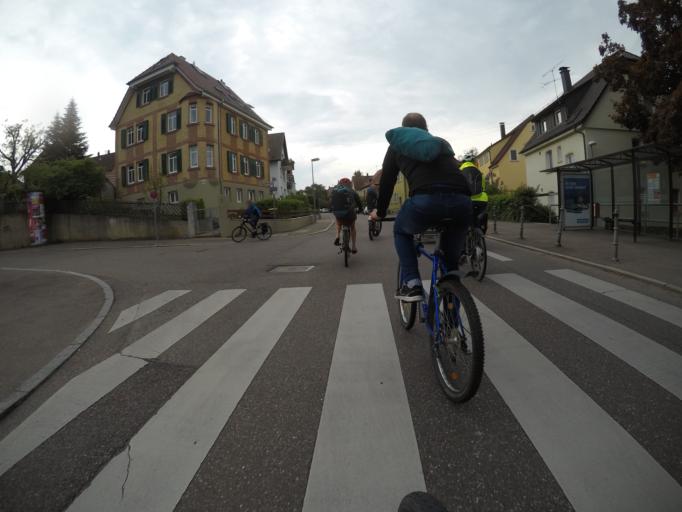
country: DE
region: Baden-Wuerttemberg
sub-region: Regierungsbezirk Stuttgart
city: Esslingen
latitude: 48.7349
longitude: 9.3272
